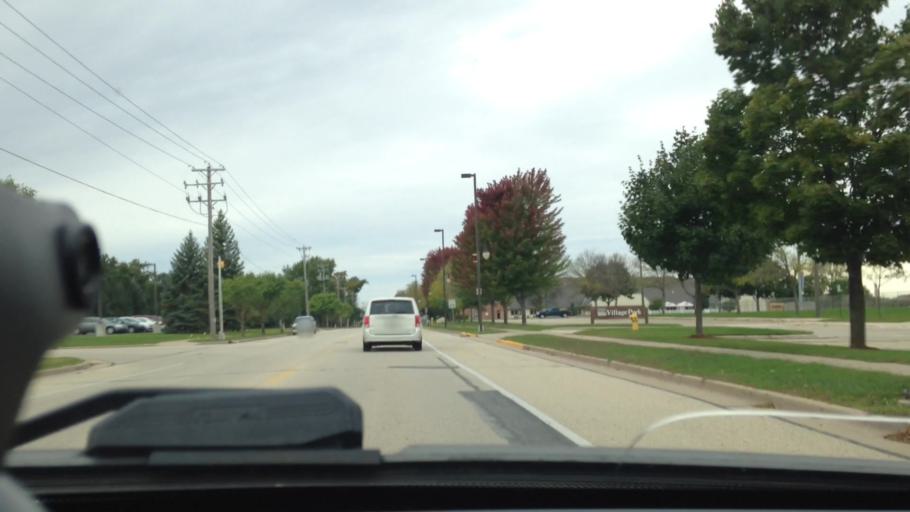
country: US
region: Wisconsin
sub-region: Fond du Lac County
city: North Fond du Lac
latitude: 43.8065
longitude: -88.4869
